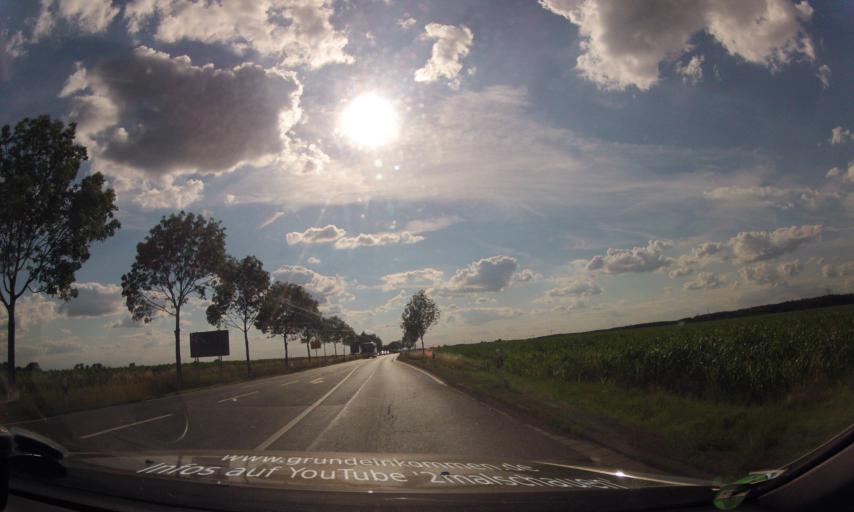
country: DE
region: Saxony
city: Machern
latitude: 51.3598
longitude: 12.6155
